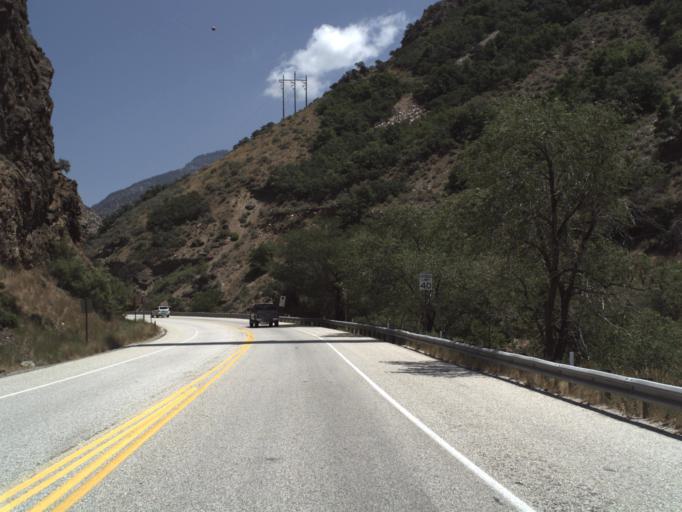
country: US
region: Utah
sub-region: Weber County
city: Ogden
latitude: 41.2367
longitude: -111.9283
